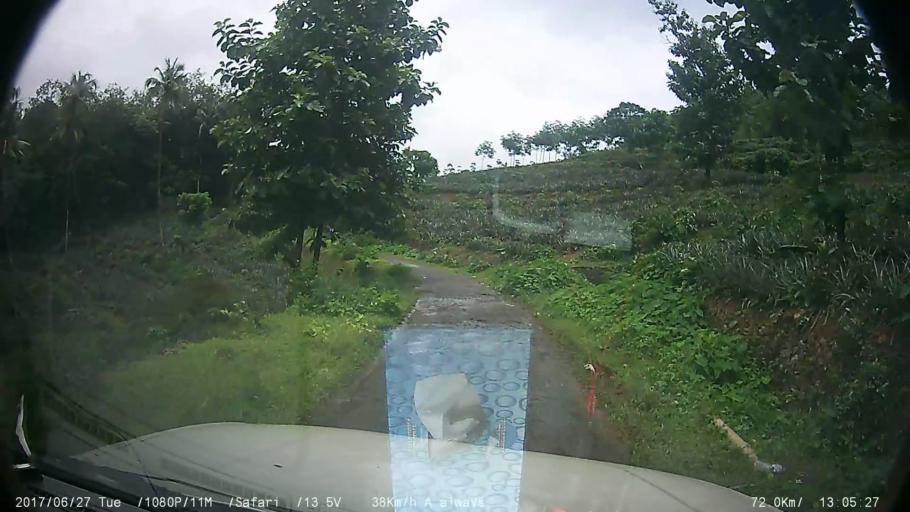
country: IN
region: Kerala
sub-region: Kottayam
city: Palackattumala
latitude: 9.7840
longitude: 76.5498
